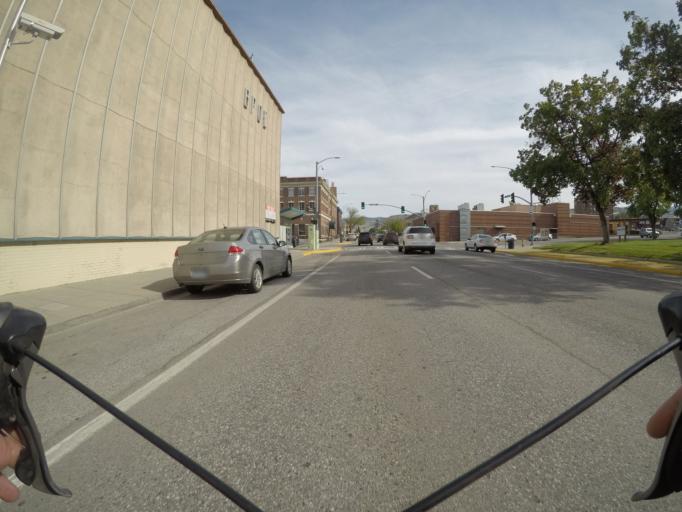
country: US
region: Washington
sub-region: Chelan County
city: Wenatchee
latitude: 47.4229
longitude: -120.3131
